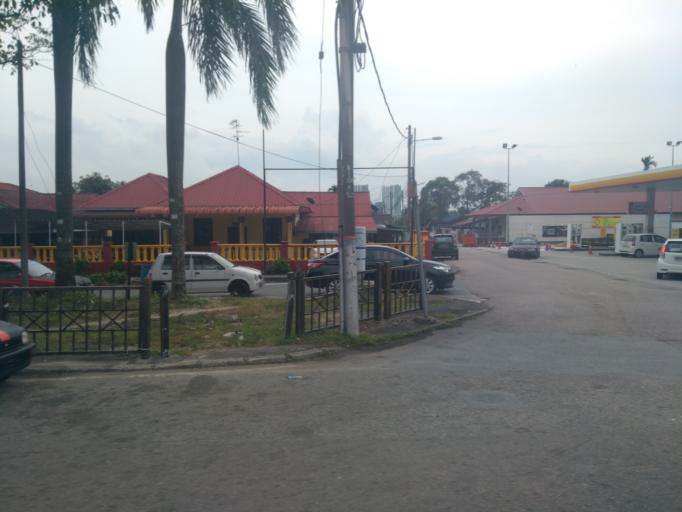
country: MY
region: Johor
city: Skudai
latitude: 1.4970
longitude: 103.7008
